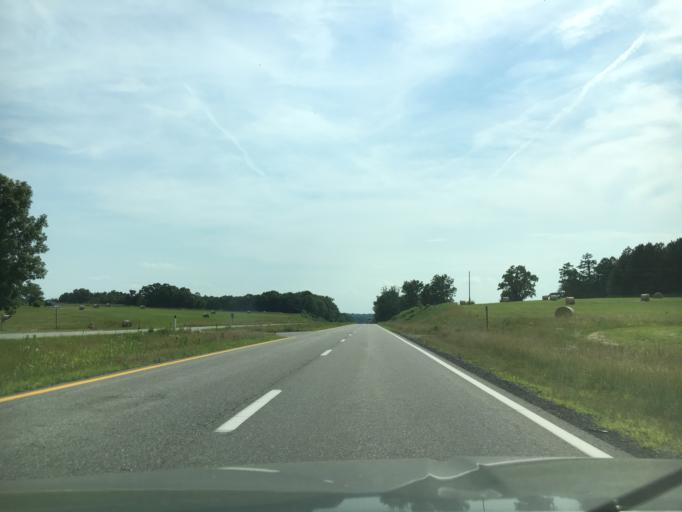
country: US
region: Virginia
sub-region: Mecklenburg County
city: Chase City
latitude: 36.8510
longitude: -78.6122
